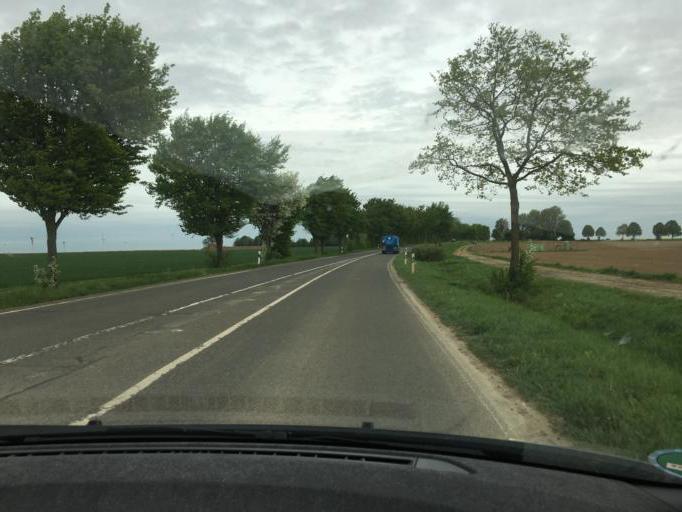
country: DE
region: North Rhine-Westphalia
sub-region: Regierungsbezirk Koln
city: Titz
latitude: 51.0522
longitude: 6.4290
